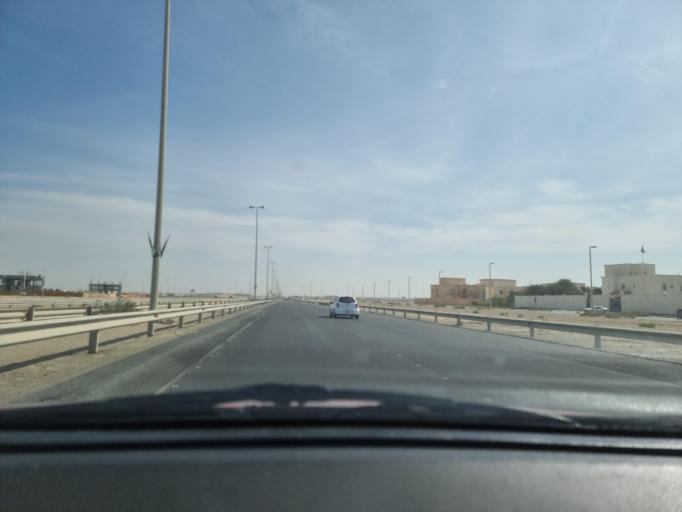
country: AE
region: Abu Dhabi
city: Abu Dhabi
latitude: 24.3630
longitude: 54.6631
